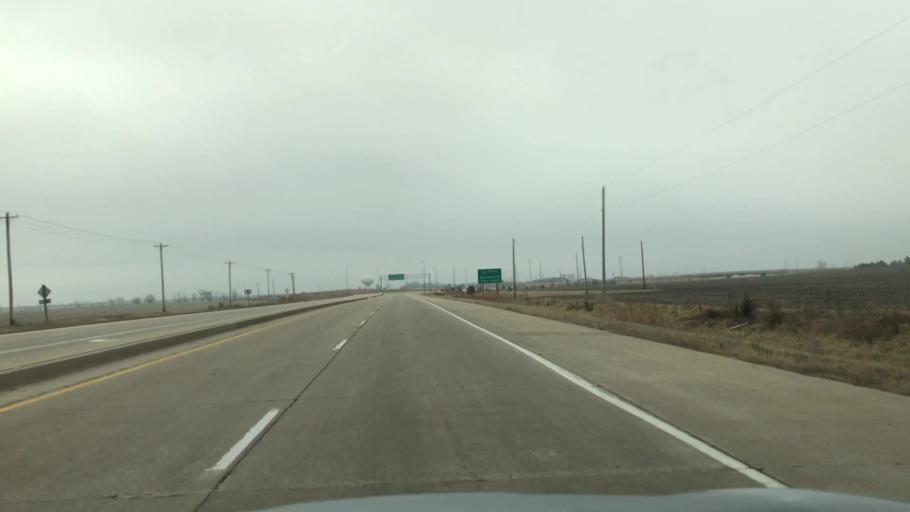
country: US
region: Illinois
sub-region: McLean County
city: Normal
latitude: 40.5466
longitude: -88.9443
